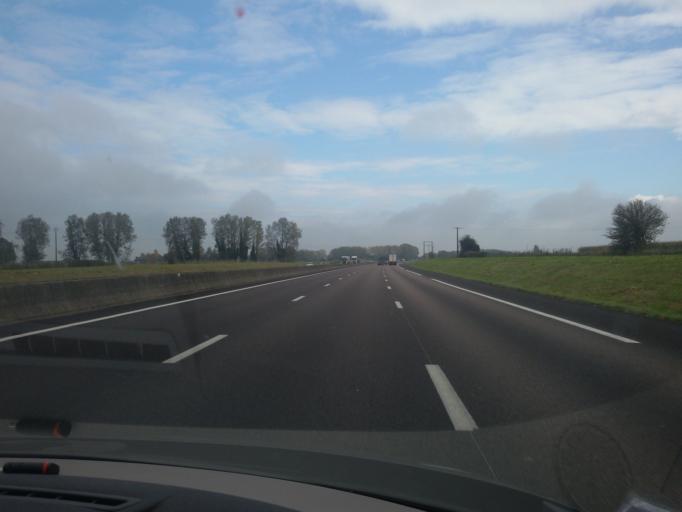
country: FR
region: Haute-Normandie
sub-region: Departement de l'Eure
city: Hauville
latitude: 49.3698
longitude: 0.7651
